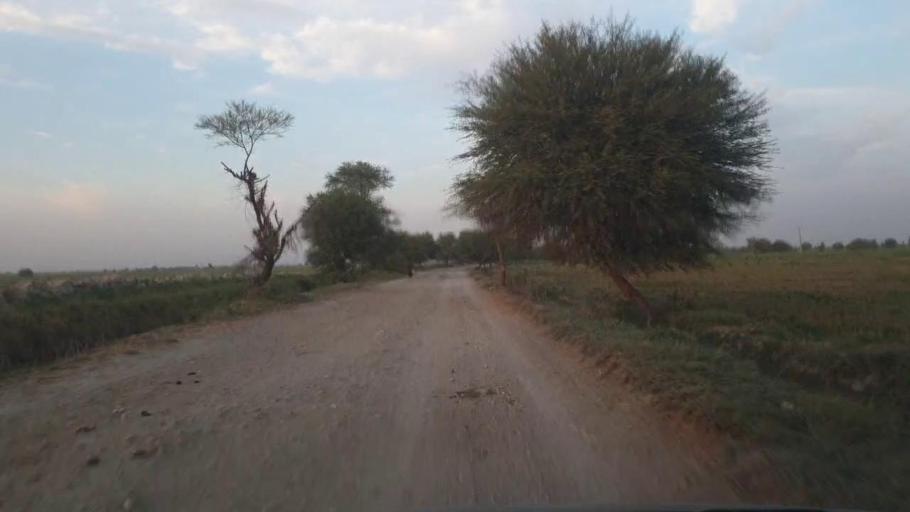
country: PK
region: Sindh
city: Umarkot
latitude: 25.2701
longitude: 69.6784
